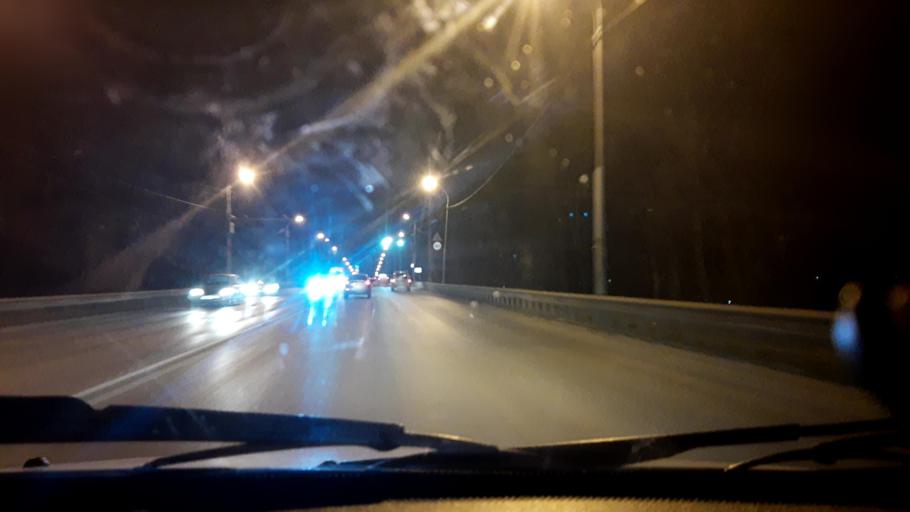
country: RU
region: Bashkortostan
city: Iglino
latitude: 54.7902
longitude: 56.2144
